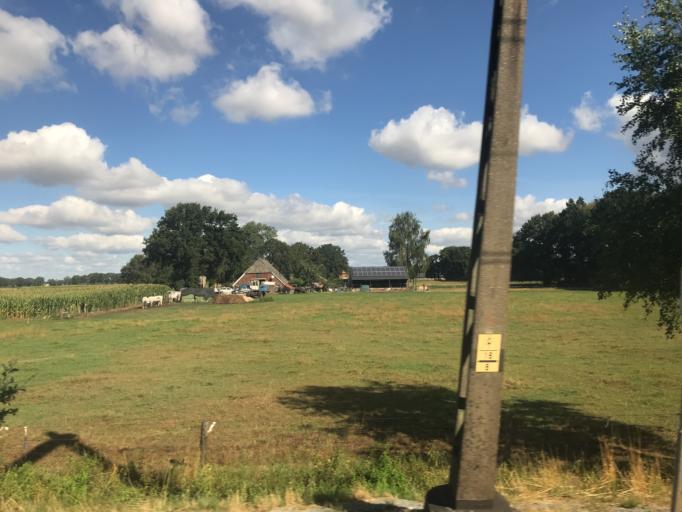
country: NL
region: Gelderland
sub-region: Gemeente Lochem
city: Laren
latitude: 52.2777
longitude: 6.3852
